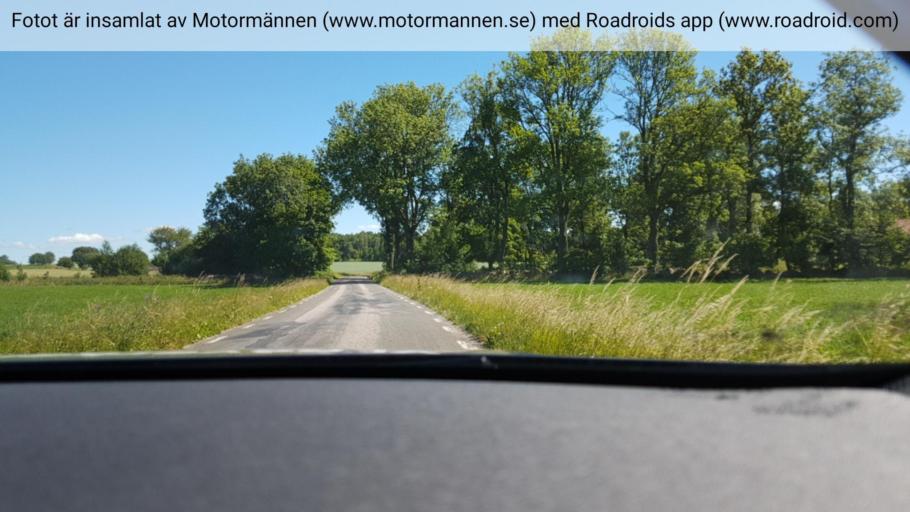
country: SE
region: Vaestra Goetaland
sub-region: Tidaholms Kommun
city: Tidaholm
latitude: 58.1951
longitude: 13.8170
